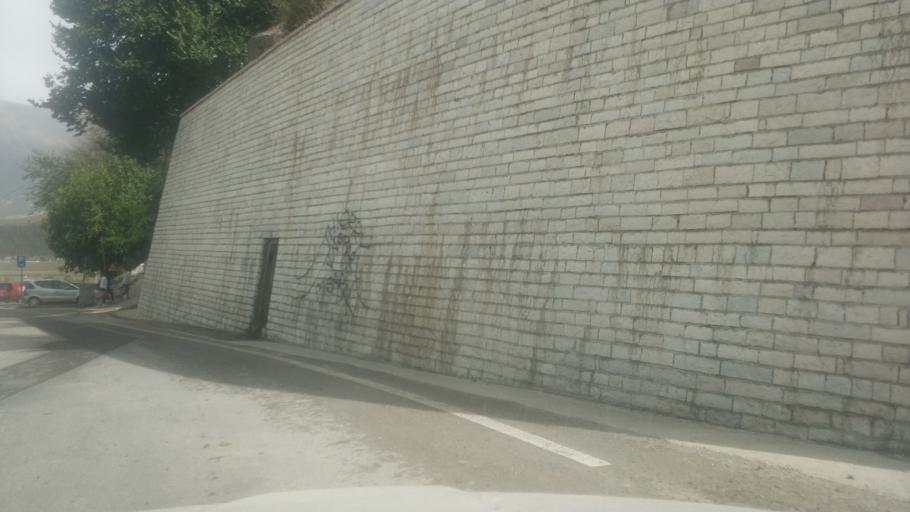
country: AL
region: Gjirokaster
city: Gjirokaster
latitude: 40.0759
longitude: 20.1463
